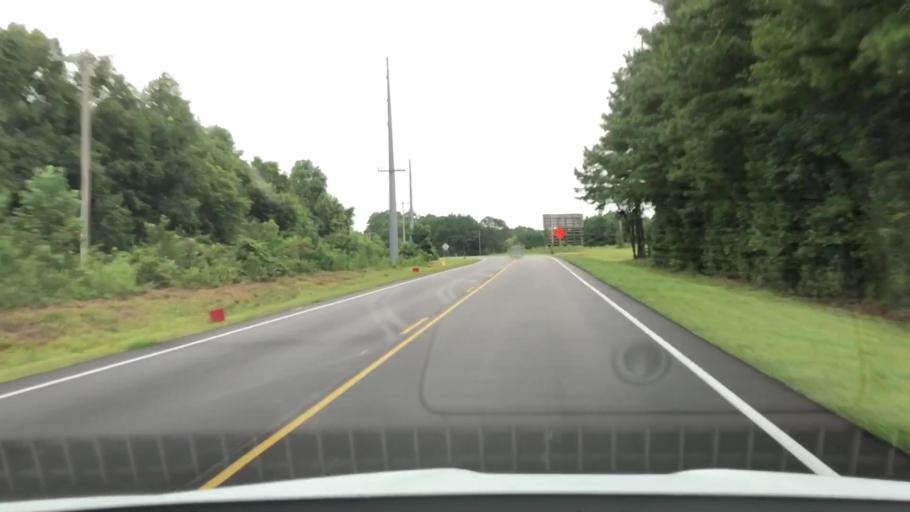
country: US
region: North Carolina
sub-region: Onslow County
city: Swansboro
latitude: 34.8005
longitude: -77.1318
